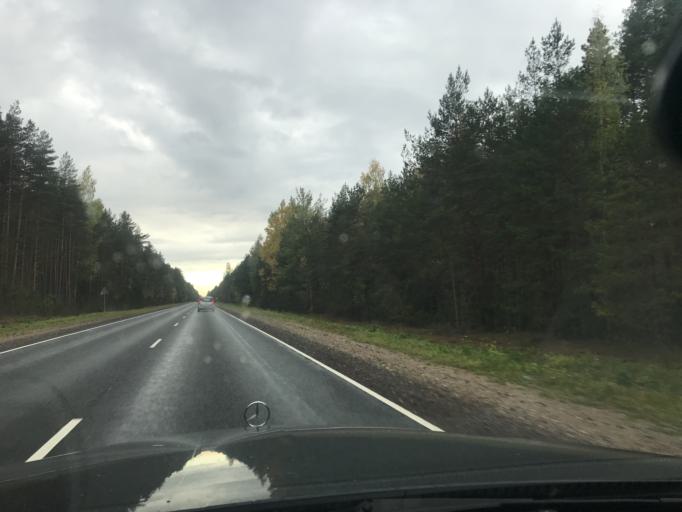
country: RU
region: Pskov
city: Izborsk
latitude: 57.7027
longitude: 27.7790
